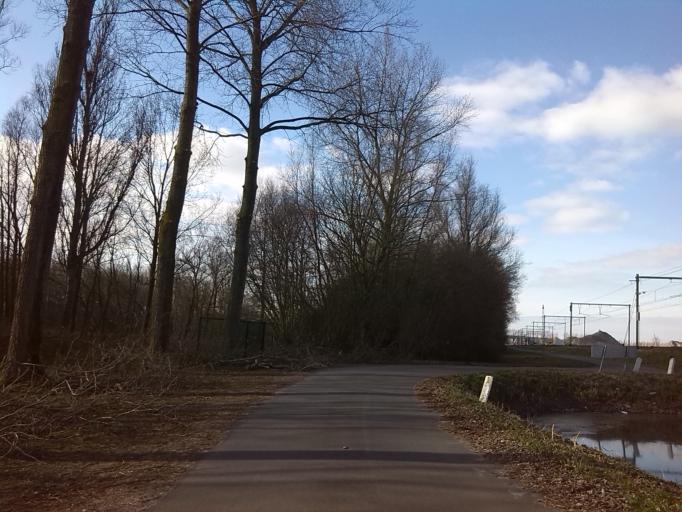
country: BE
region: Flanders
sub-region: Provincie West-Vlaanderen
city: Zuienkerke
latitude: 51.2558
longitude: 3.2000
